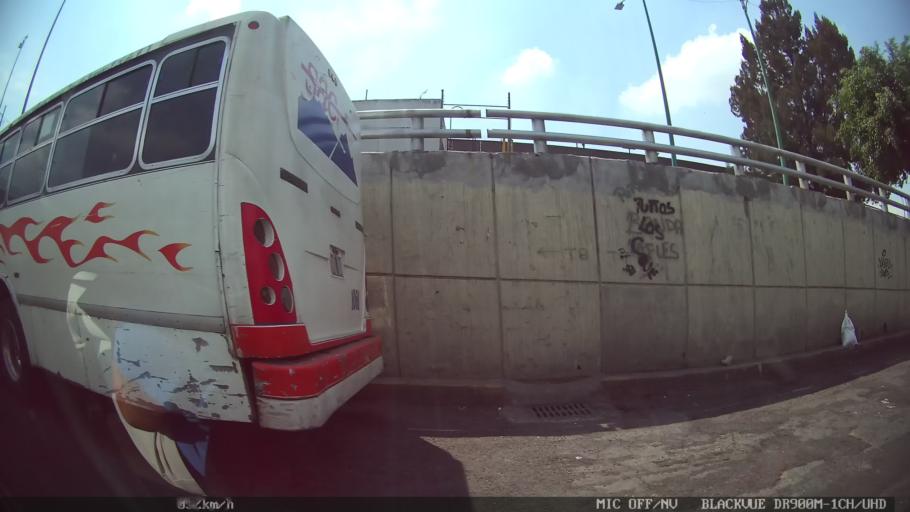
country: MX
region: Mexico City
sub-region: Iztacalco
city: Iztacalco
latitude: 19.4139
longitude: -99.0736
